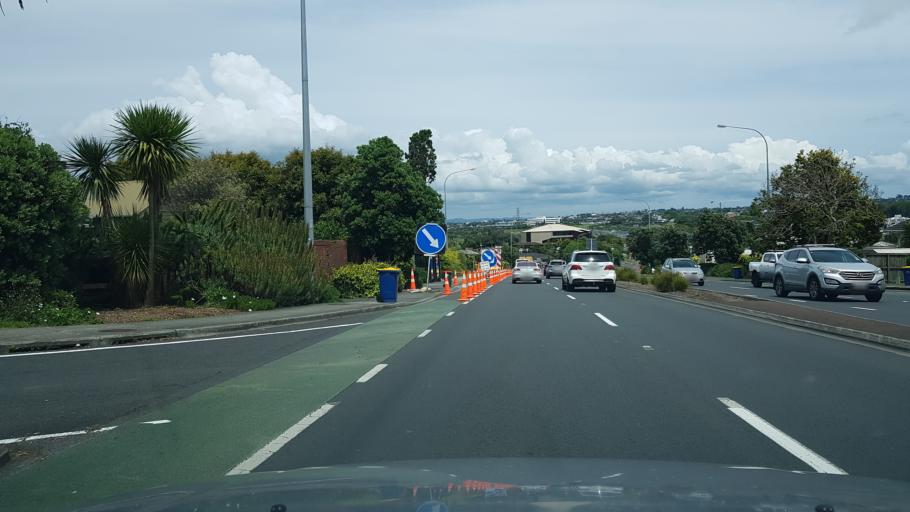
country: NZ
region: Auckland
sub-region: Auckland
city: North Shore
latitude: -36.7948
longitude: 174.7728
